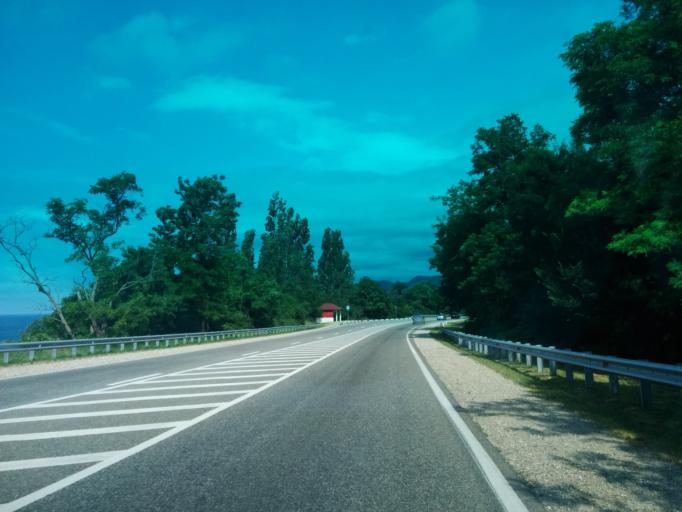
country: RU
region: Krasnodarskiy
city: Nebug
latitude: 44.1549
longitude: 39.0068
